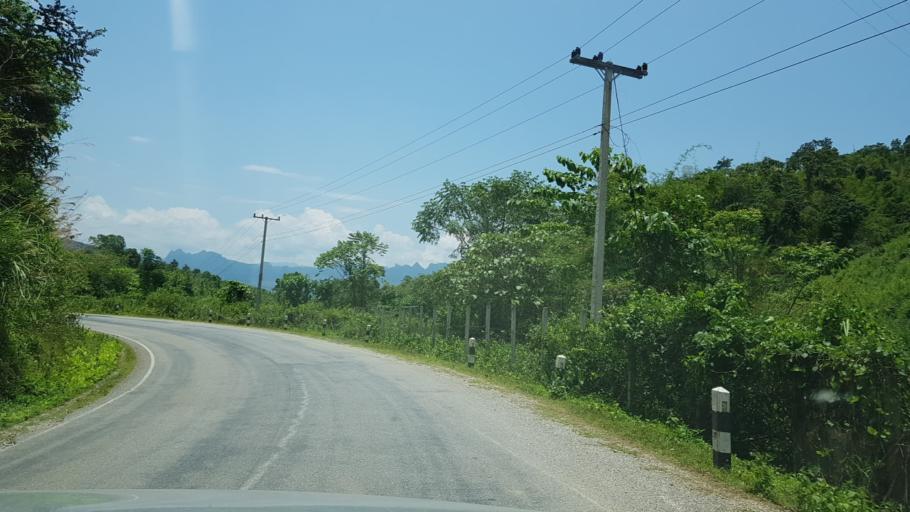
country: LA
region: Vientiane
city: Muang Kasi
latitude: 19.2706
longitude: 102.2117
